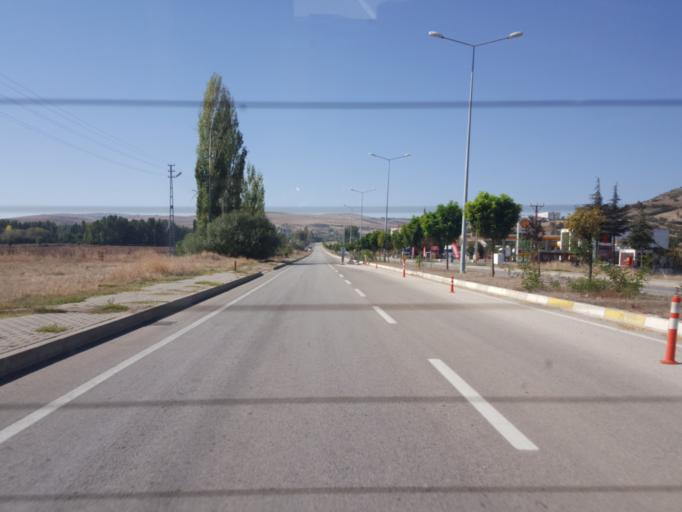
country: TR
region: Tokat
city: Zile
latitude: 40.2876
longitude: 35.8646
